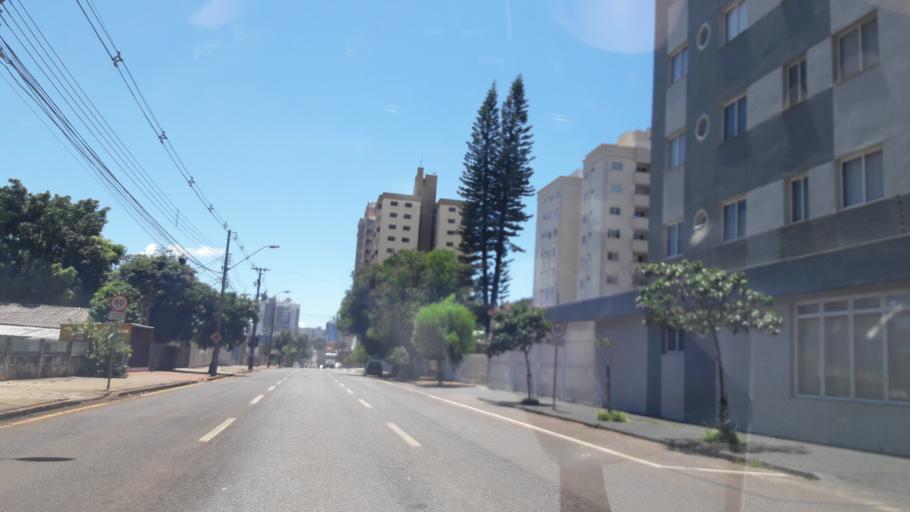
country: BR
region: Parana
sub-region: Cascavel
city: Cascavel
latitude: -24.9512
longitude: -53.4738
